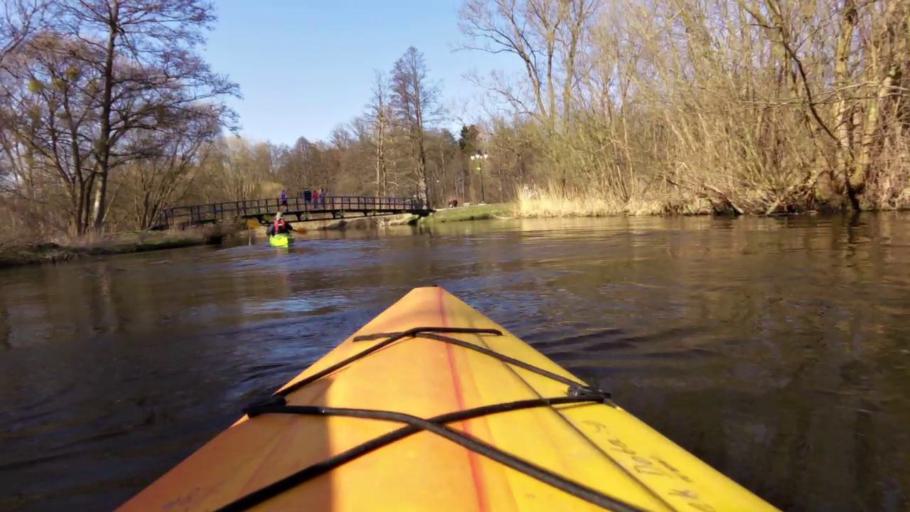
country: PL
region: West Pomeranian Voivodeship
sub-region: Powiat lobeski
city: Resko
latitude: 53.7681
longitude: 15.4072
